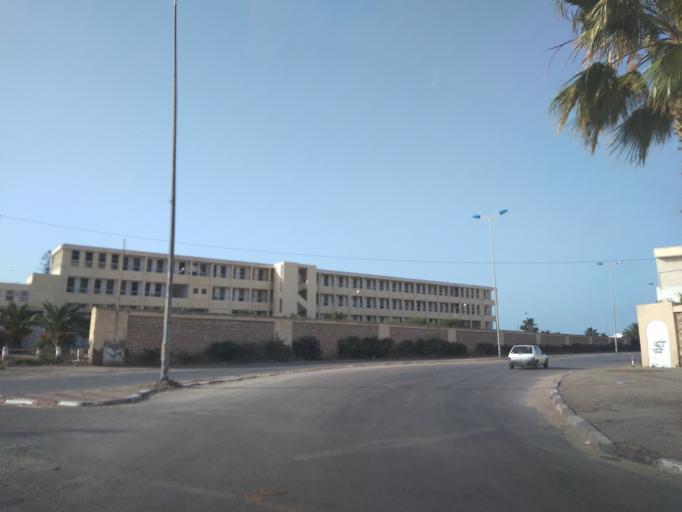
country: TN
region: Safaqis
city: Sfax
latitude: 34.7341
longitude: 10.7482
